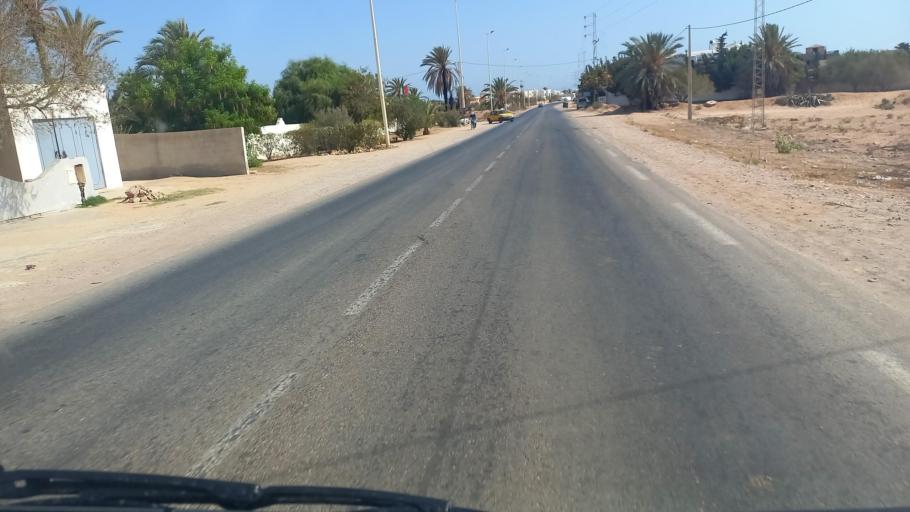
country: TN
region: Madanin
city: Midoun
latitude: 33.7730
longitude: 11.0272
